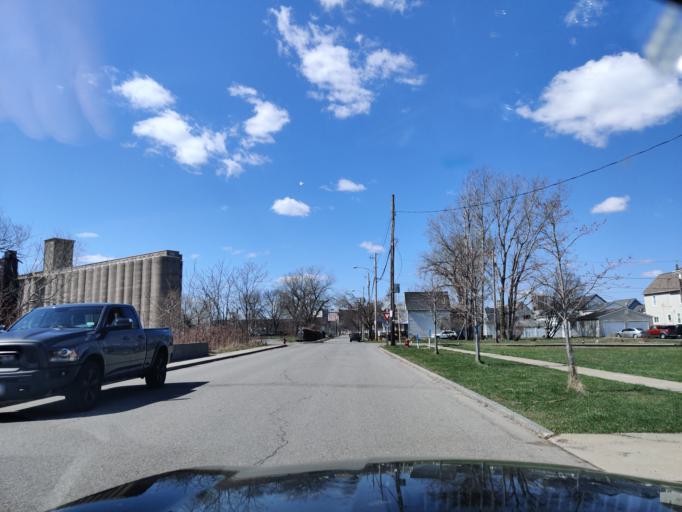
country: US
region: New York
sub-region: Erie County
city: Buffalo
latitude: 42.8643
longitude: -78.8612
